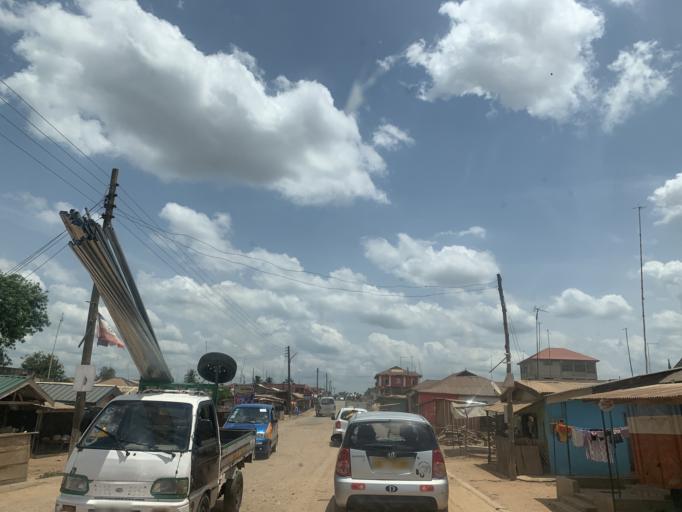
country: GH
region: Central
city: Swedru
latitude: 5.5093
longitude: -0.6935
